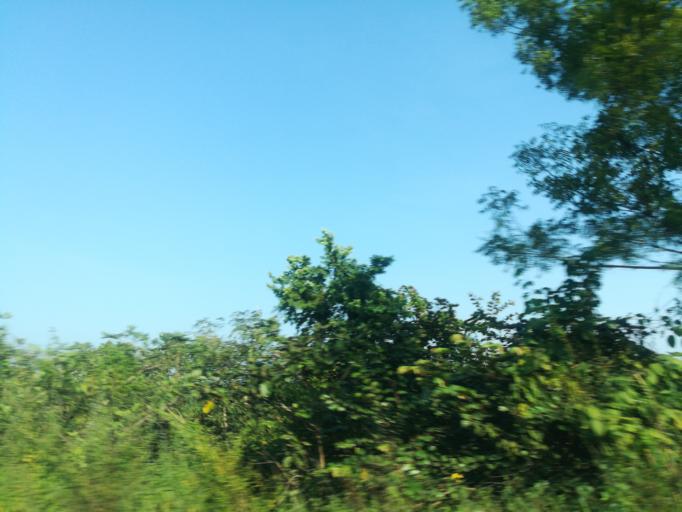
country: NG
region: Ogun
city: Abeokuta
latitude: 7.2519
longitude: 3.3005
